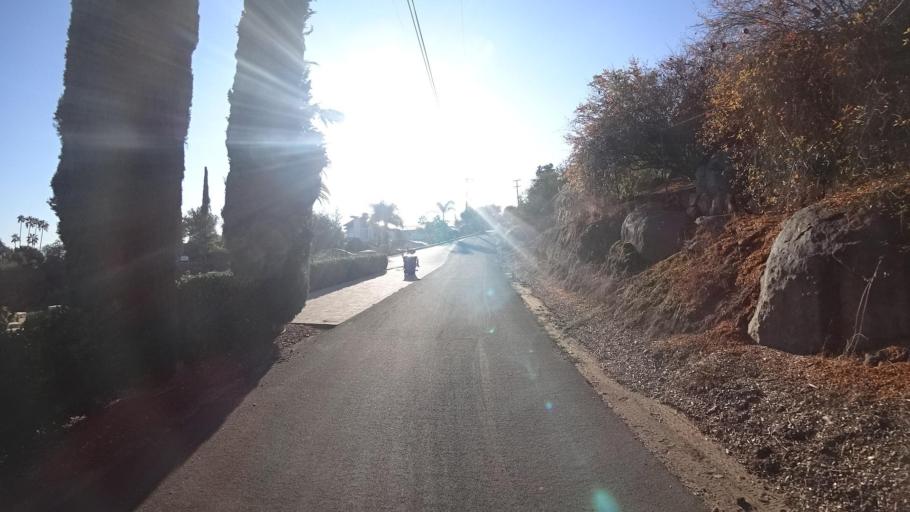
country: US
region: California
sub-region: San Diego County
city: Casa de Oro-Mount Helix
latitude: 32.7721
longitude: -116.9633
